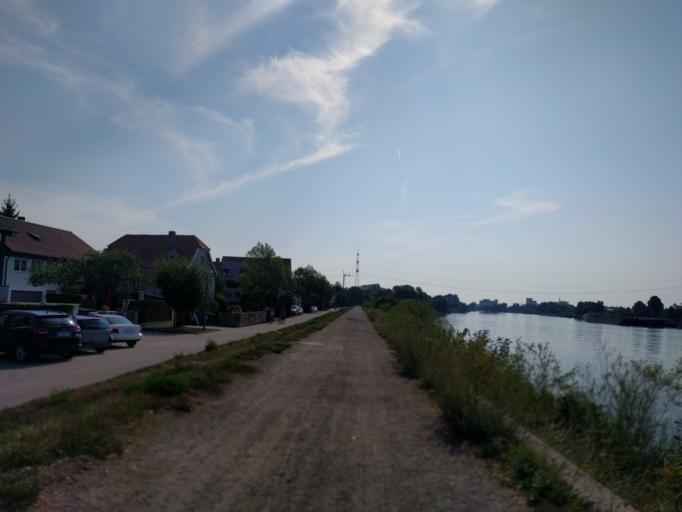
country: DE
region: Bavaria
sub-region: Upper Palatinate
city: Regensburg
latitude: 49.0229
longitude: 12.1457
